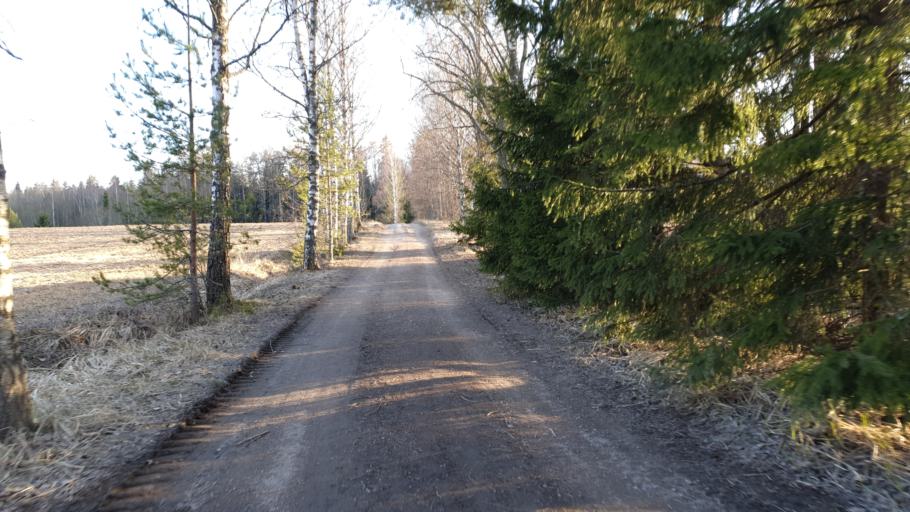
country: FI
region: Uusimaa
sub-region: Helsinki
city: Nurmijaervi
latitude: 60.3404
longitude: 24.8522
